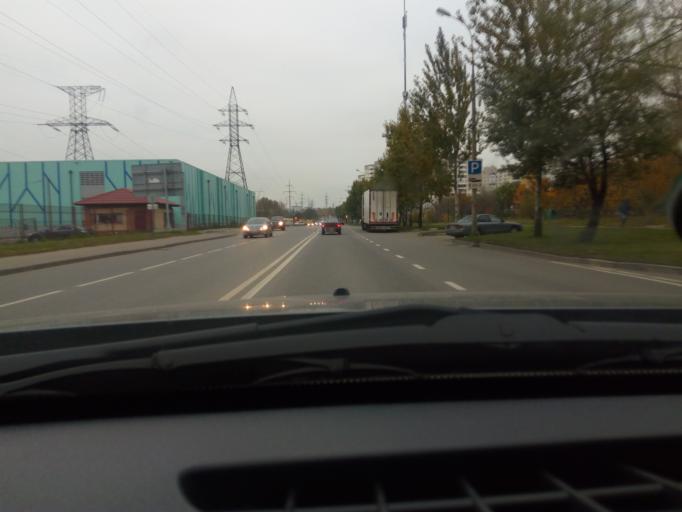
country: RU
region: Moskovskaya
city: Kuskovo
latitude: 55.7324
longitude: 37.8473
